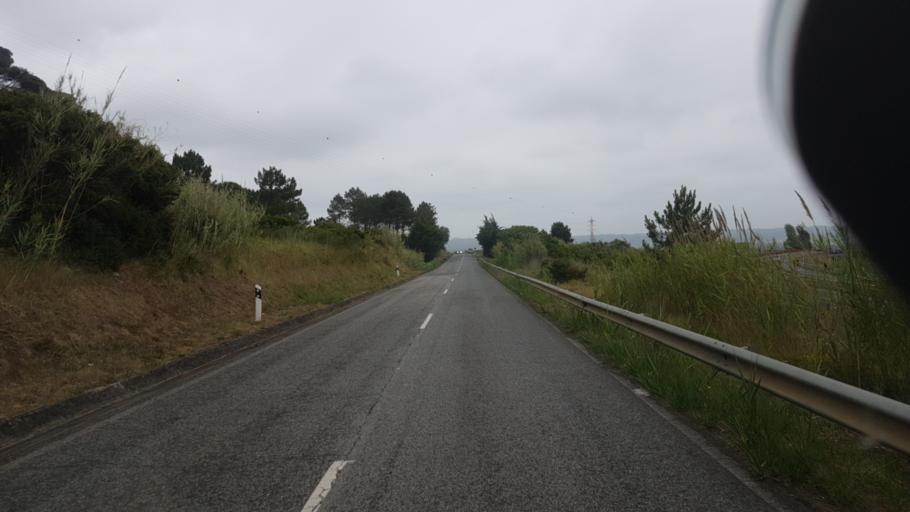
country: PT
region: Leiria
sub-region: Obidos
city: Obidos
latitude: 39.3397
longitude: -9.1711
